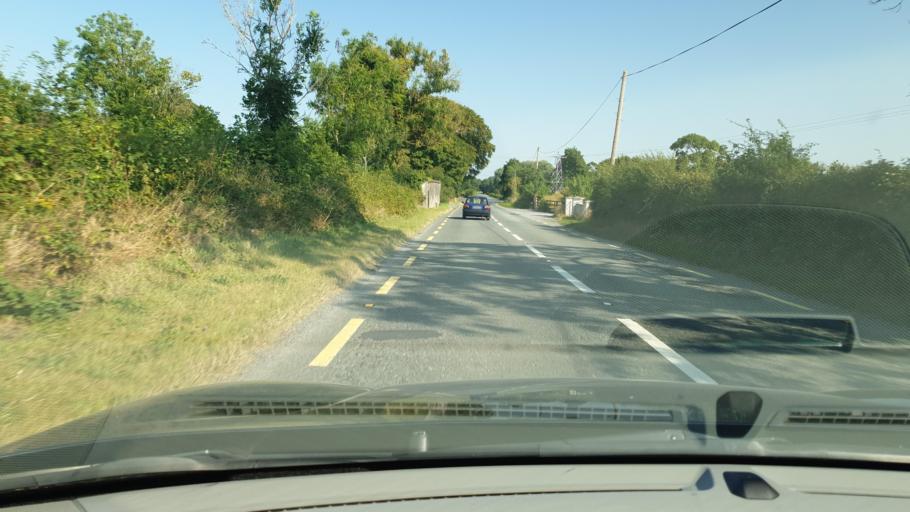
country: IE
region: Leinster
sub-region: An Mhi
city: Trim
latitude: 53.6318
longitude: -6.8000
